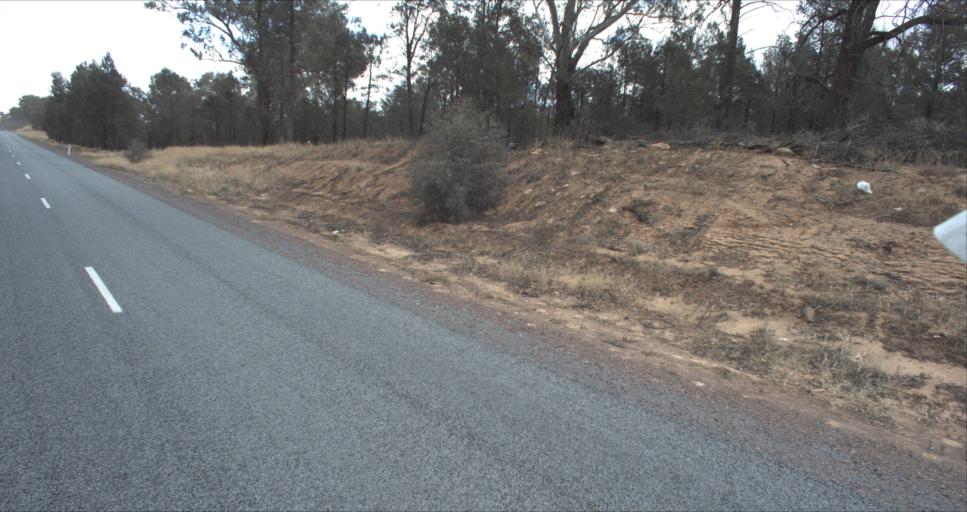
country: AU
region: New South Wales
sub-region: Leeton
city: Leeton
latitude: -34.6559
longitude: 146.3503
